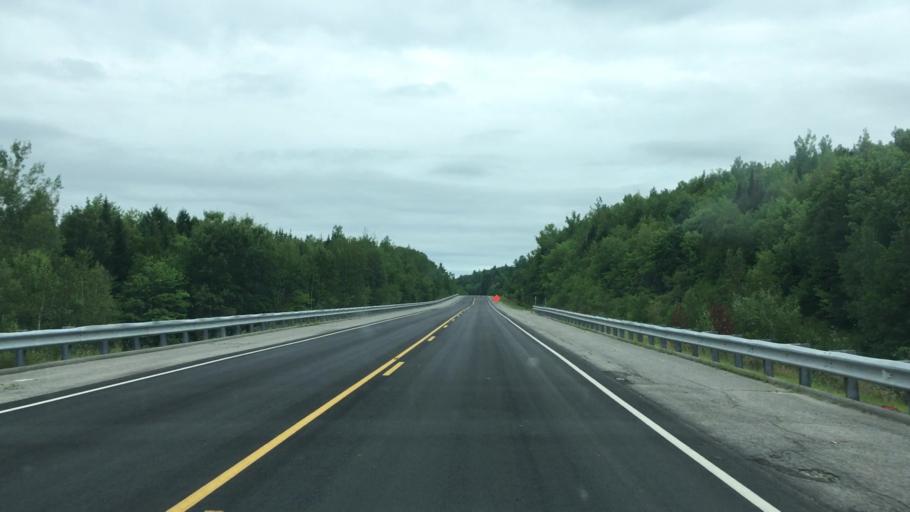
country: US
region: Maine
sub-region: Washington County
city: Cherryfield
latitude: 44.8896
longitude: -67.8565
